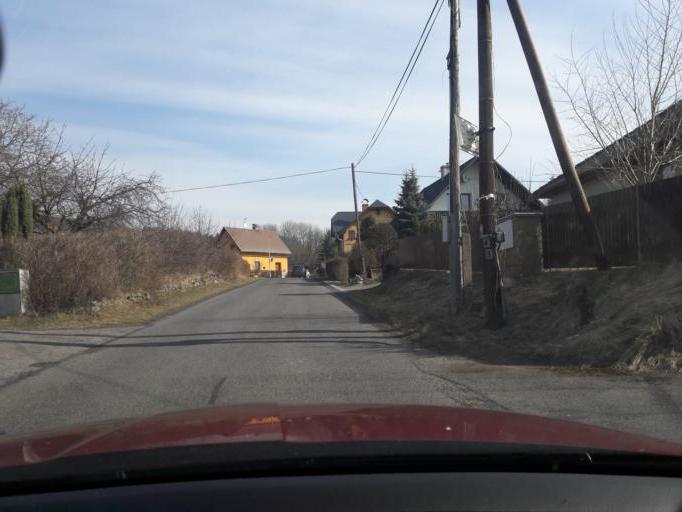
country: CZ
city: Novy Bor
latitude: 50.7676
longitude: 14.5292
